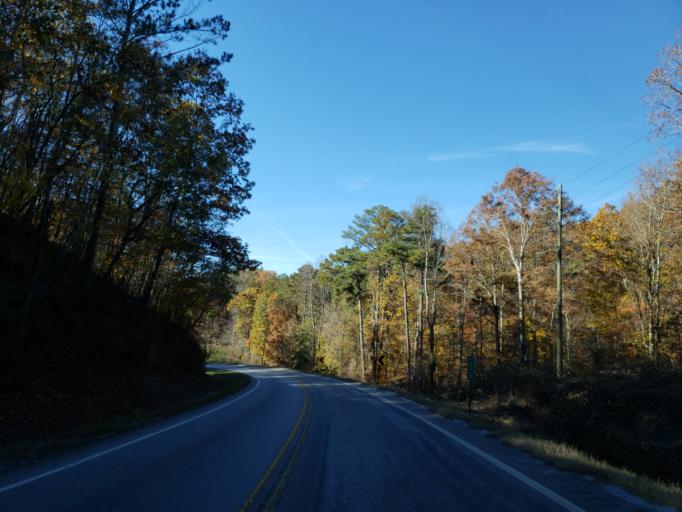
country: US
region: Alabama
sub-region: Calhoun County
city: Choccolocco
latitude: 33.5896
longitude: -85.6847
